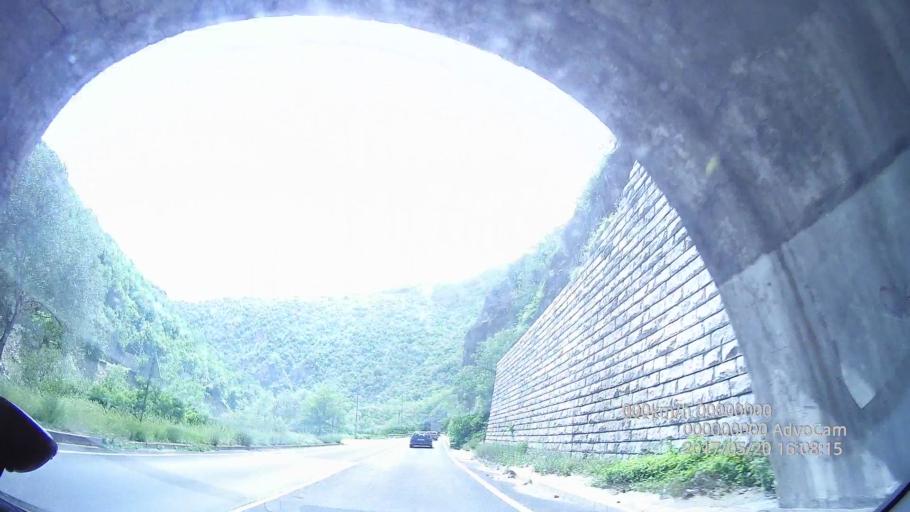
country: BG
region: Blagoevgrad
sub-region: Obshtina Kresna
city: Stara Kresna
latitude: 41.7905
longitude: 23.1579
